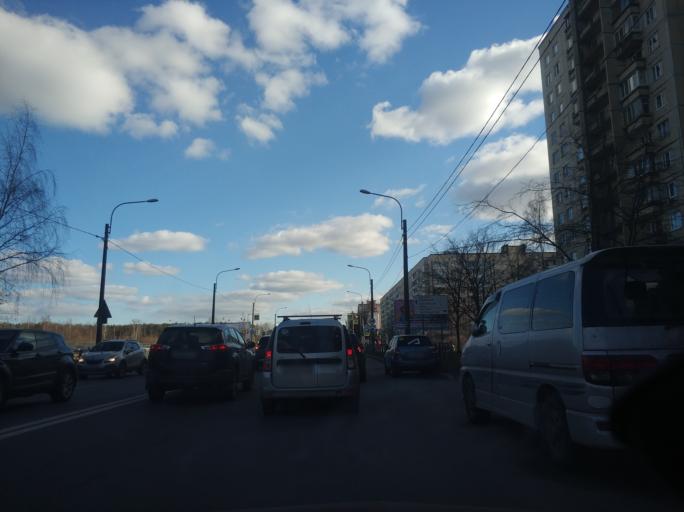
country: RU
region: St.-Petersburg
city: Krasnogvargeisky
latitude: 59.9543
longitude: 30.4964
